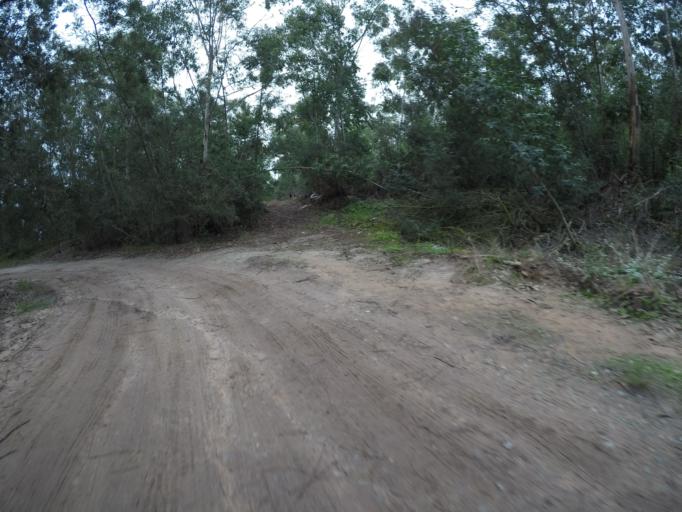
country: ZA
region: Western Cape
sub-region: Eden District Municipality
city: Knysna
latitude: -34.0103
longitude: 22.8061
